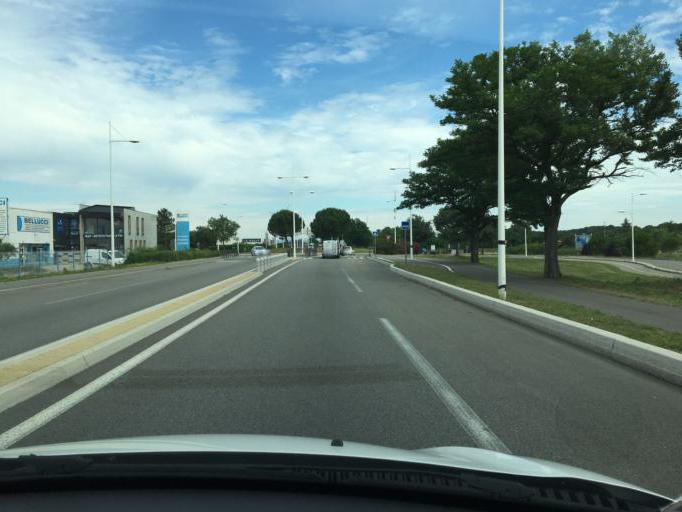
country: FR
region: Provence-Alpes-Cote d'Azur
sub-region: Departement du Vaucluse
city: Bollene
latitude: 44.2977
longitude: 4.7509
